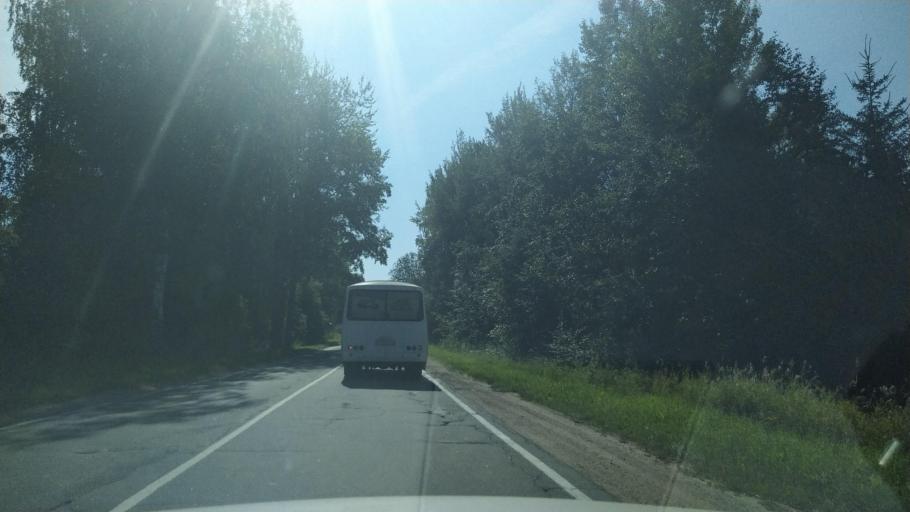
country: RU
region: Leningrad
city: Siverskiy
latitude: 59.3311
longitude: 30.0611
